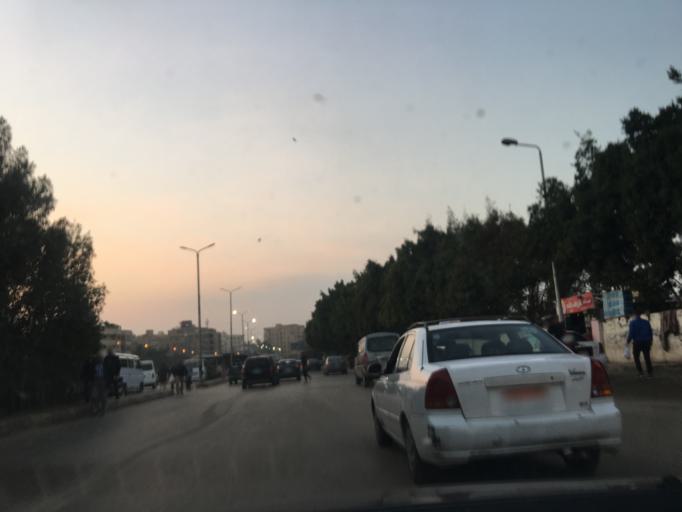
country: EG
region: Al Jizah
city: Al Jizah
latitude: 29.9902
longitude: 31.1343
